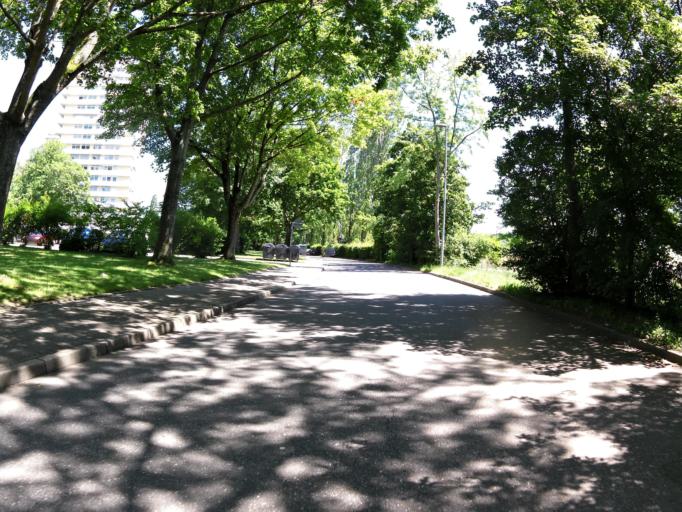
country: DE
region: Baden-Wuerttemberg
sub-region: Freiburg Region
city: Lahr
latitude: 48.3347
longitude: 7.8353
